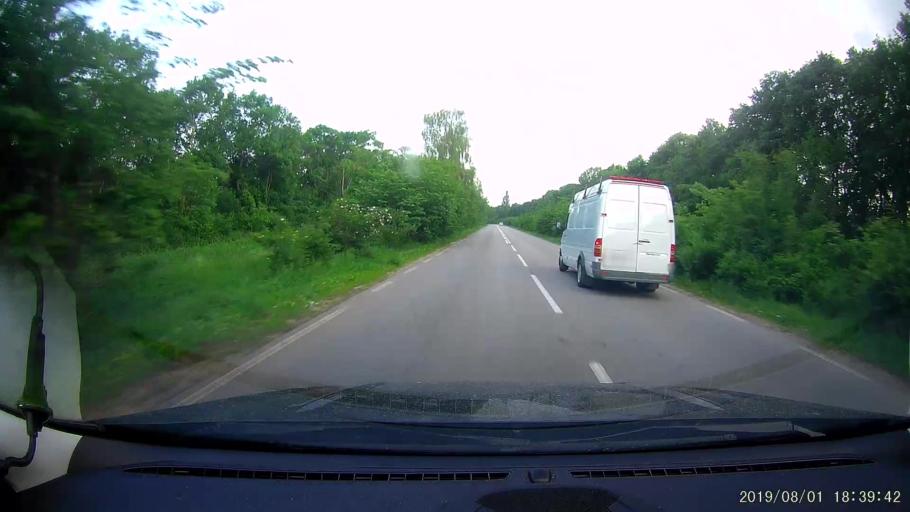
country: BG
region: Shumen
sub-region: Obshtina Khitrino
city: Gara Khitrino
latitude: 43.3802
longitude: 26.9174
